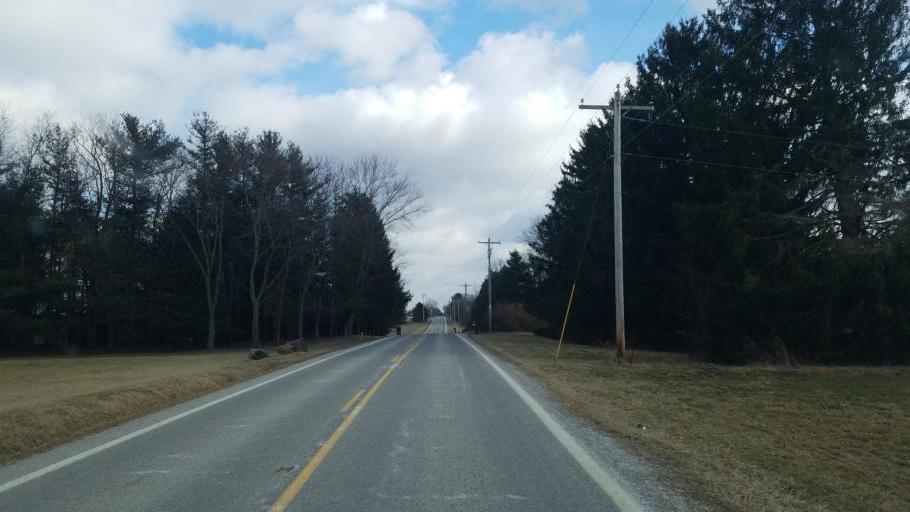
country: US
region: Ohio
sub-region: Morrow County
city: Mount Gilead
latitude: 40.5829
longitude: -82.7369
